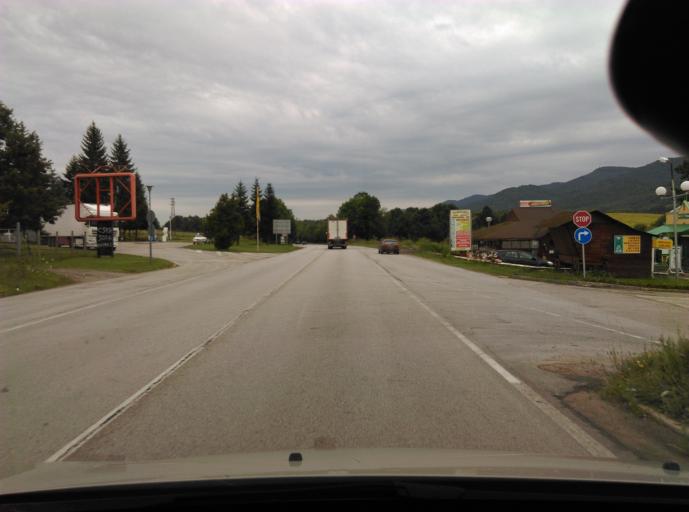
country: BG
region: Lovech
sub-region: Obshtina Ugurchin
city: Ugurchin
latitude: 43.0402
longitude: 24.5303
